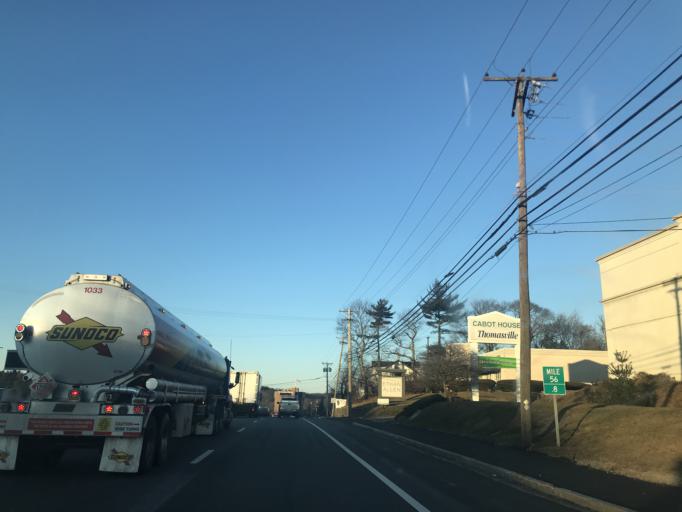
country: US
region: Massachusetts
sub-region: Essex County
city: Saugus
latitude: 42.4756
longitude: -71.0235
